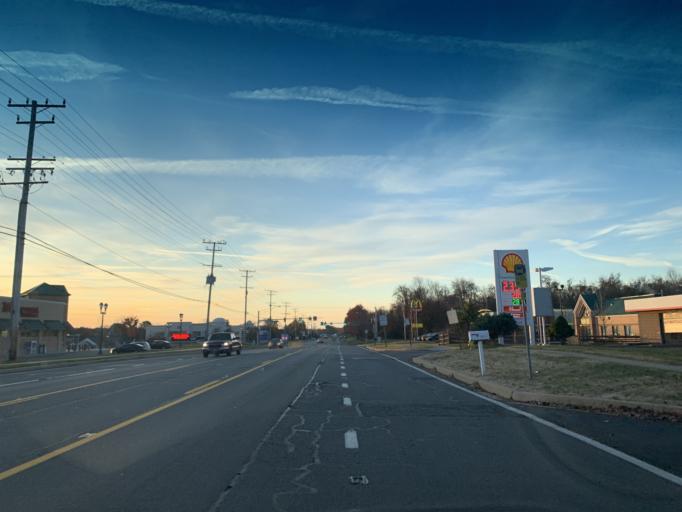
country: US
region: Maryland
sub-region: Harford County
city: Bel Air South
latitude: 39.5038
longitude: -76.3274
